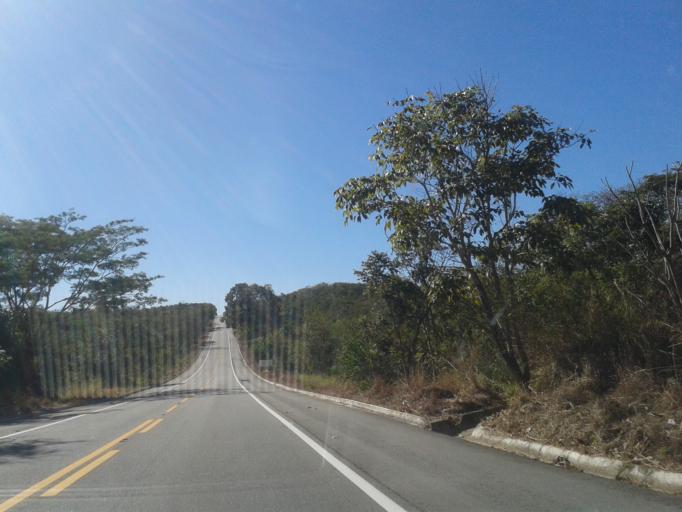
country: BR
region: Goias
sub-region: Goias
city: Goias
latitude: -15.7333
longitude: -50.1844
